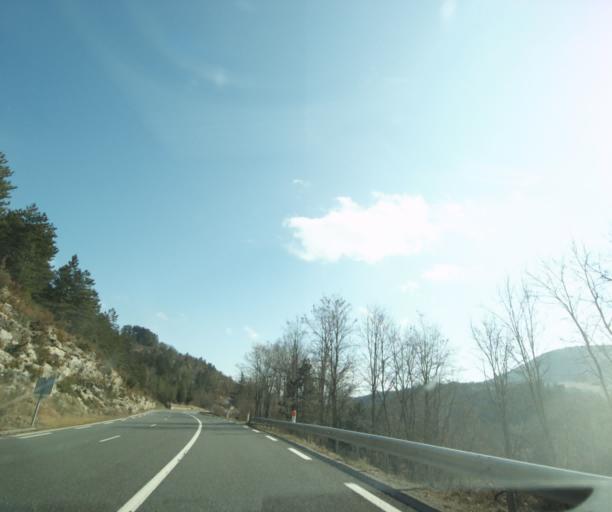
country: FR
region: Languedoc-Roussillon
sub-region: Departement de la Lozere
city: Chirac
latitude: 44.4853
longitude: 3.2935
